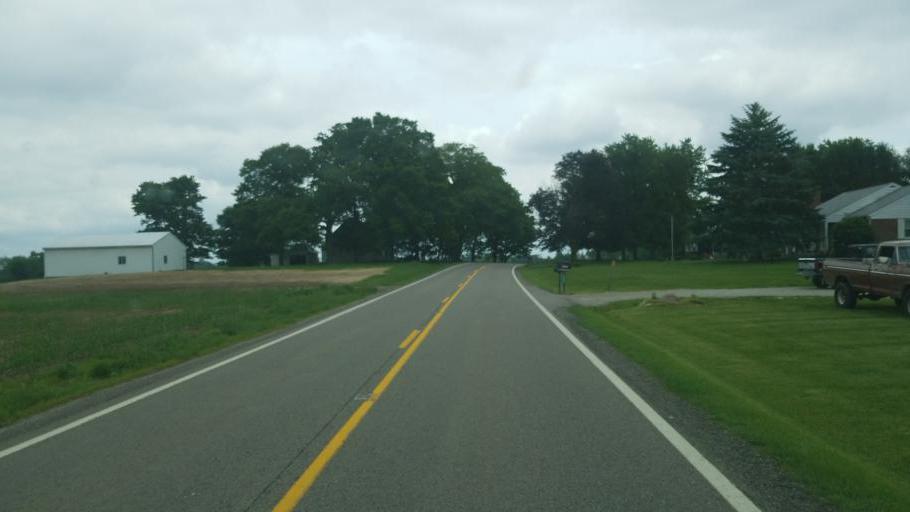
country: US
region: Ohio
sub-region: Fairfield County
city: Millersport
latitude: 39.8408
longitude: -82.5324
